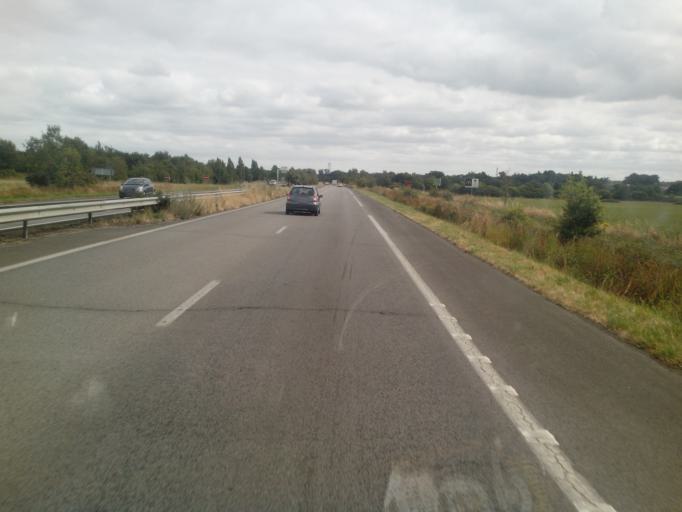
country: FR
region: Pays de la Loire
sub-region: Departement de la Loire-Atlantique
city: Heric
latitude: 47.4389
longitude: -1.6399
